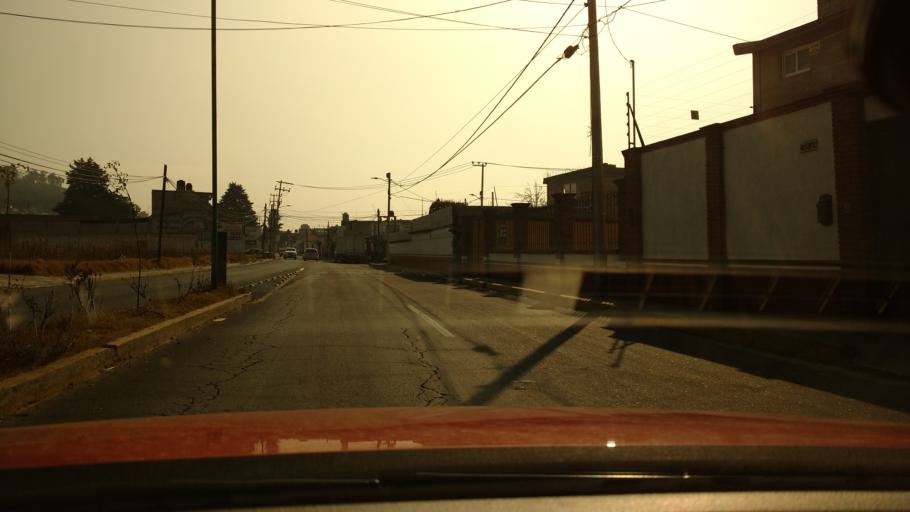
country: MX
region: Morelos
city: Chapultepec
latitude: 19.2035
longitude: -99.5659
